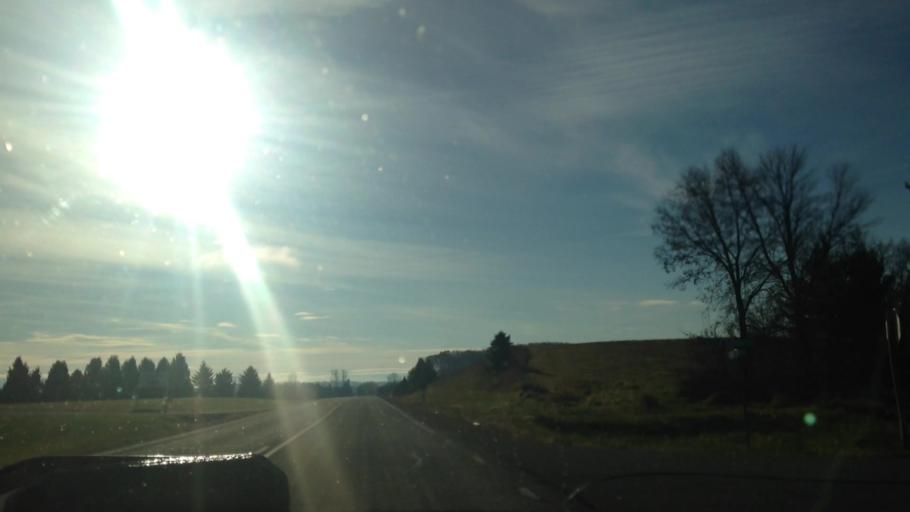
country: US
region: Wisconsin
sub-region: Dodge County
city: Mayville
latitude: 43.4864
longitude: -88.5136
